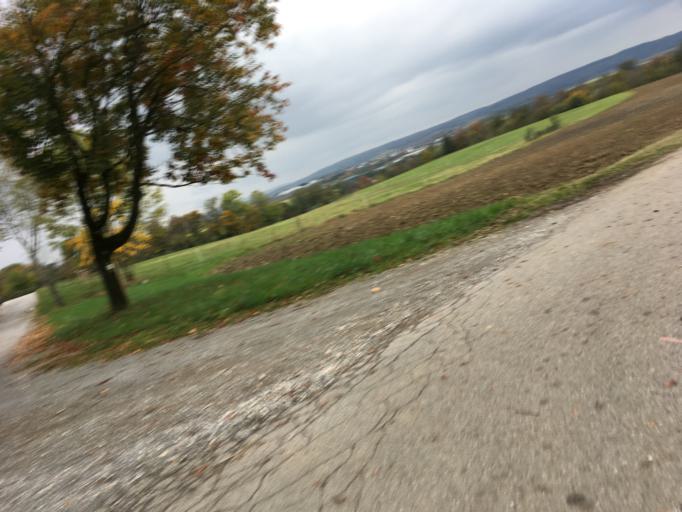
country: DE
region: Baden-Wuerttemberg
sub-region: Tuebingen Region
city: Gomaringen
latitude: 48.4410
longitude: 9.0976
